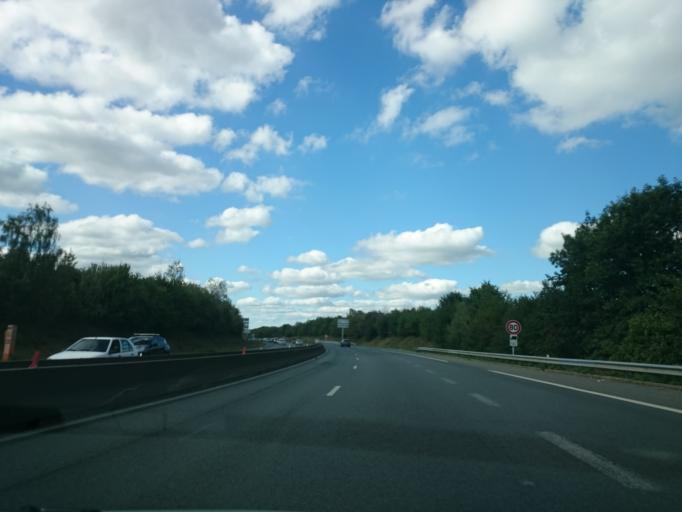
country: FR
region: Pays de la Loire
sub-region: Departement de la Loire-Atlantique
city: Saint-Herblain
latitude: 47.2286
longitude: -1.6218
